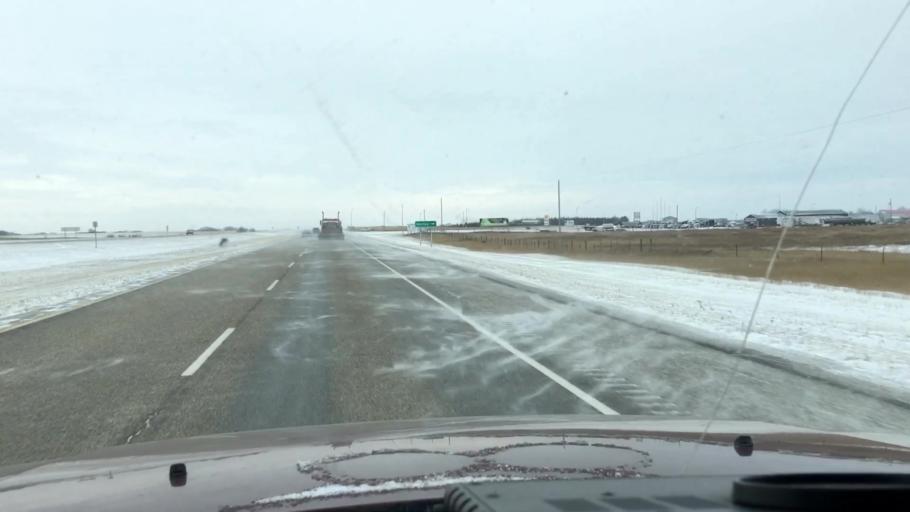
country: CA
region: Saskatchewan
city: Saskatoon
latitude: 51.6365
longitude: -106.4310
